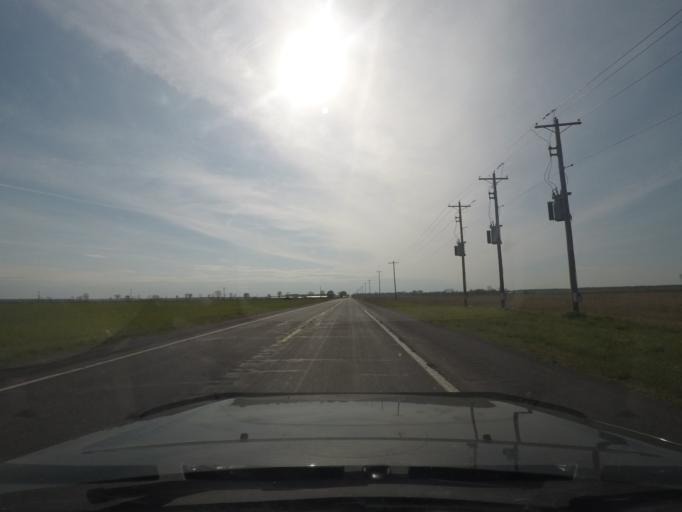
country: US
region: Michigan
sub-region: Berrien County
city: Three Oaks
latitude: 41.7983
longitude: -86.5403
